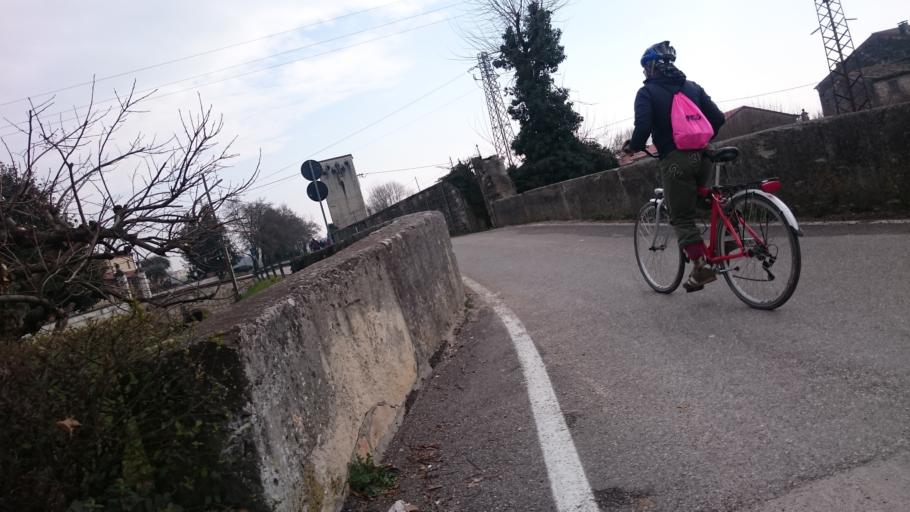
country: IT
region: Veneto
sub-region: Provincia di Vicenza
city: Lumignano
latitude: 45.4543
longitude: 11.6031
